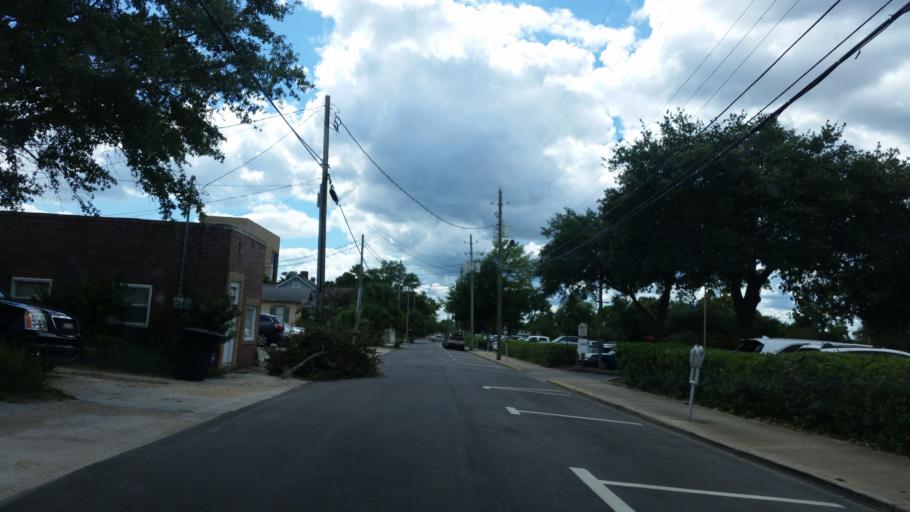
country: US
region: Florida
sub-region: Escambia County
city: Pensacola
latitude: 30.4100
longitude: -87.2166
